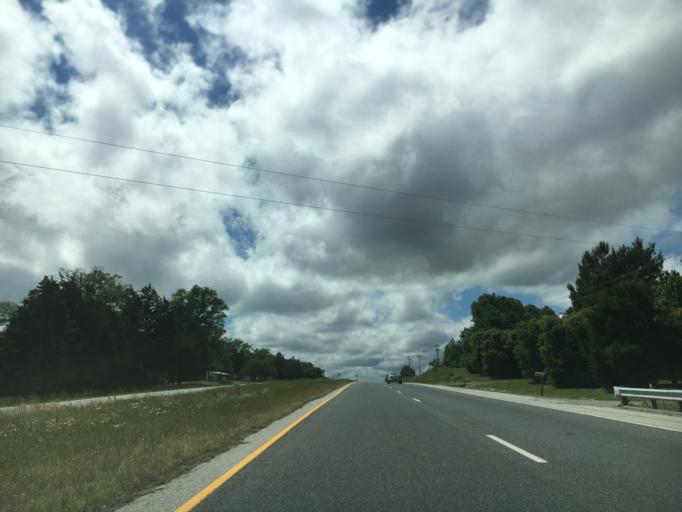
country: US
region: Virginia
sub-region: Mecklenburg County
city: Boydton
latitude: 36.6714
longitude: -78.2557
